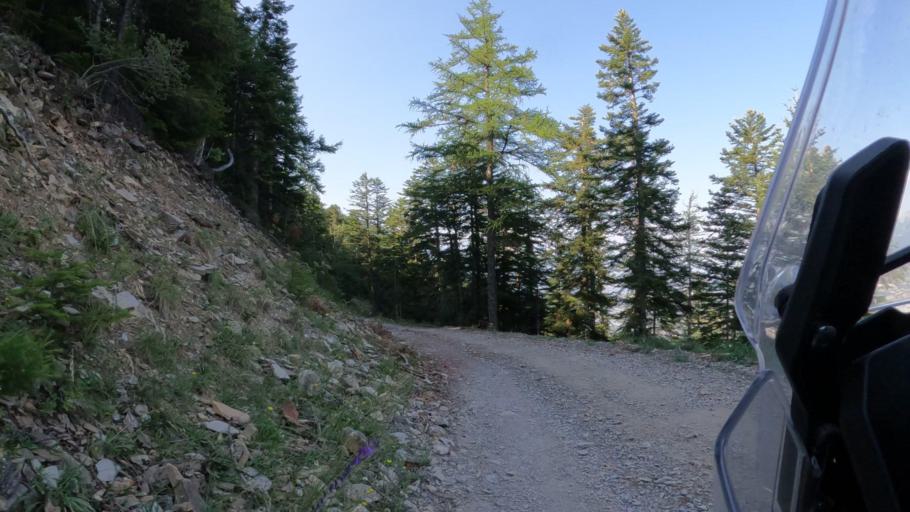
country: FR
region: Provence-Alpes-Cote d'Azur
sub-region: Departement des Hautes-Alpes
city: Embrun
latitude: 44.5914
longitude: 6.5677
